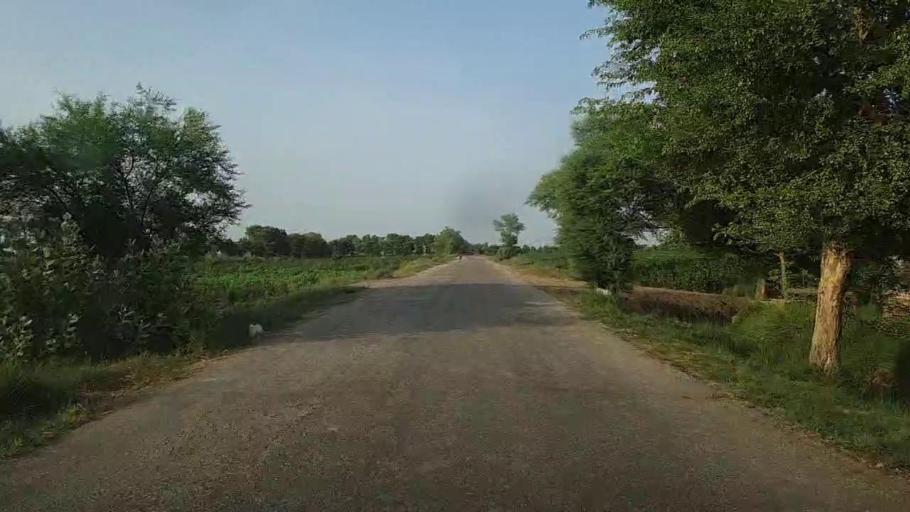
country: PK
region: Sindh
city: Ubauro
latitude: 28.1121
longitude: 69.8196
